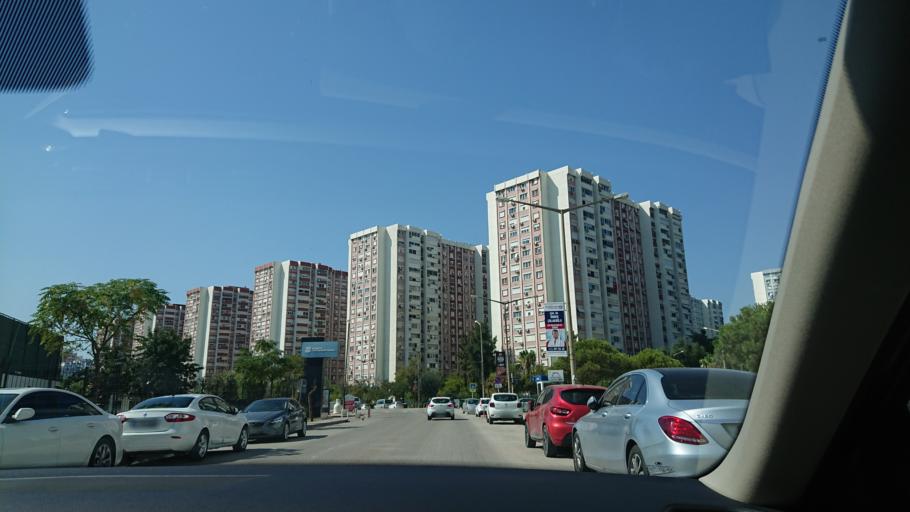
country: TR
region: Izmir
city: Karsiyaka
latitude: 38.4689
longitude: 27.0804
